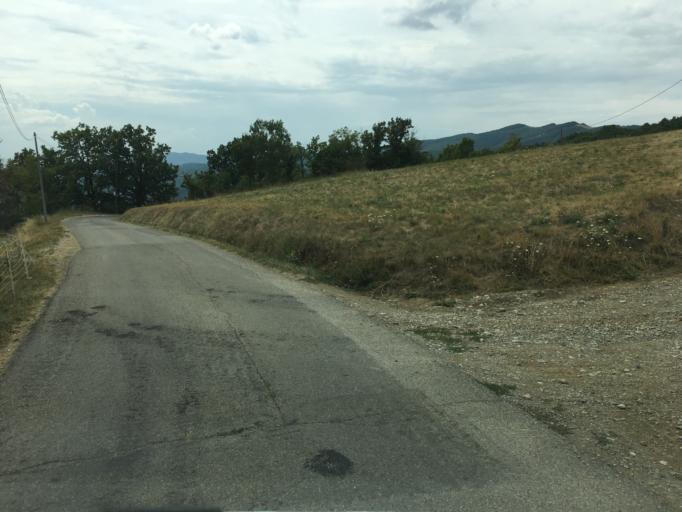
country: FR
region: Provence-Alpes-Cote d'Azur
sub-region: Departement des Alpes-de-Haute-Provence
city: Digne-les-Bains
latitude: 44.1960
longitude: 6.1351
